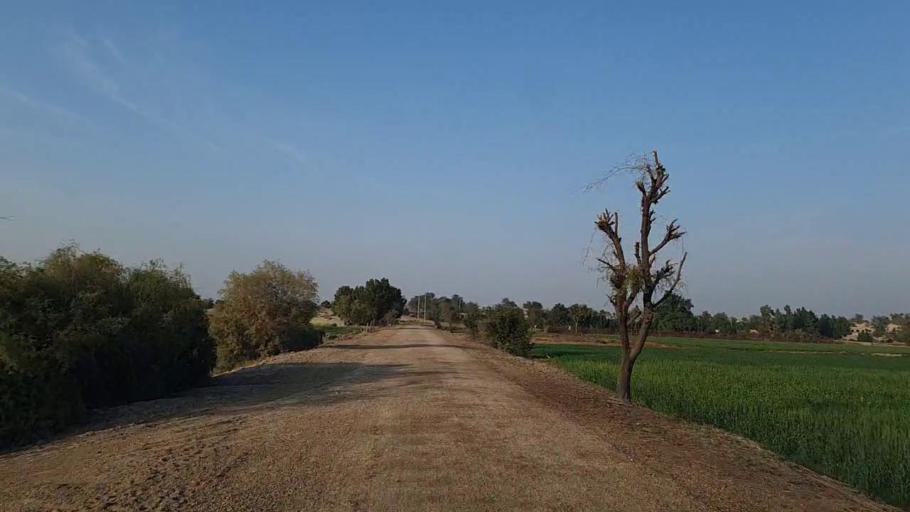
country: PK
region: Sindh
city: Jam Sahib
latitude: 26.3797
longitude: 68.5287
